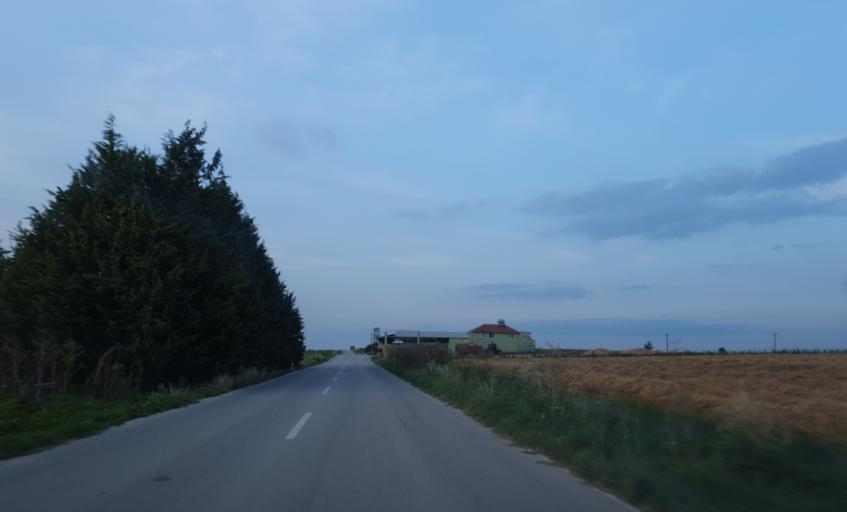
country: TR
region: Tekirdag
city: Beyazkoy
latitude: 41.3938
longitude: 27.6306
